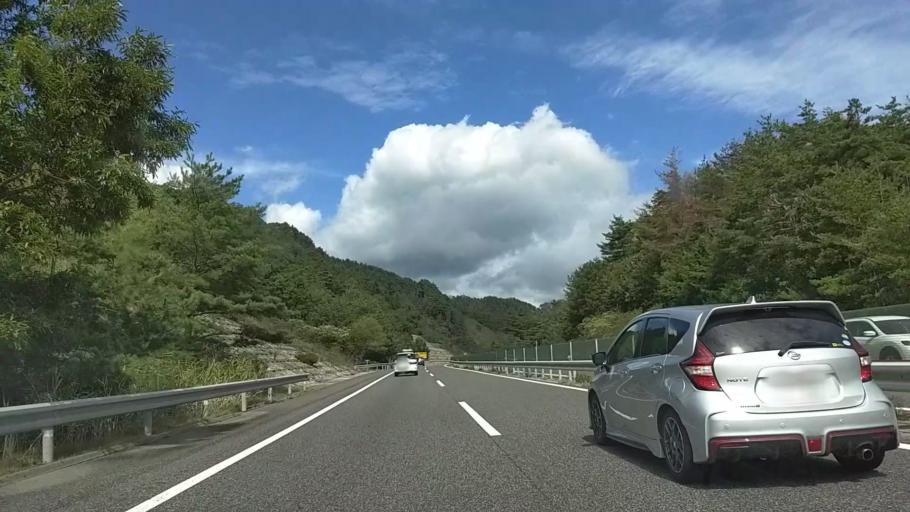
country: JP
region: Nagano
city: Hotaka
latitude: 36.3996
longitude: 138.0021
